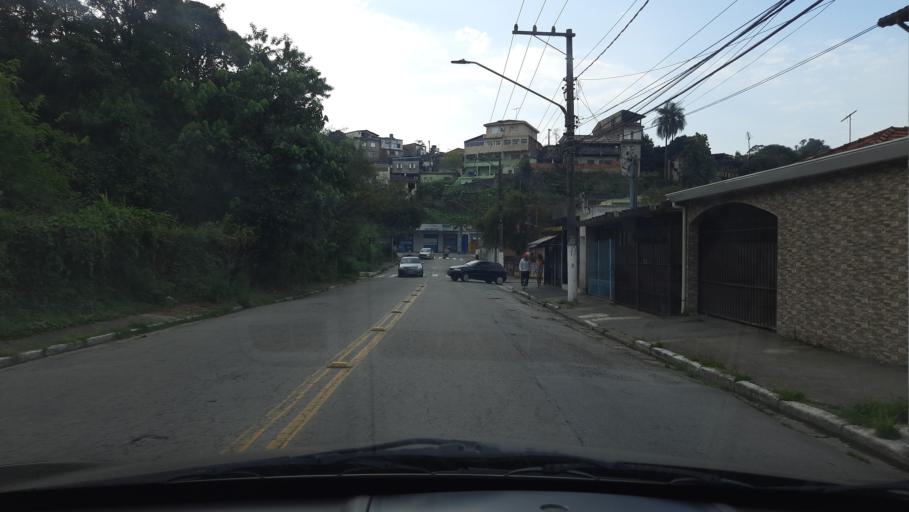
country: BR
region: Sao Paulo
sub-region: Caieiras
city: Caieiras
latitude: -23.4538
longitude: -46.7425
